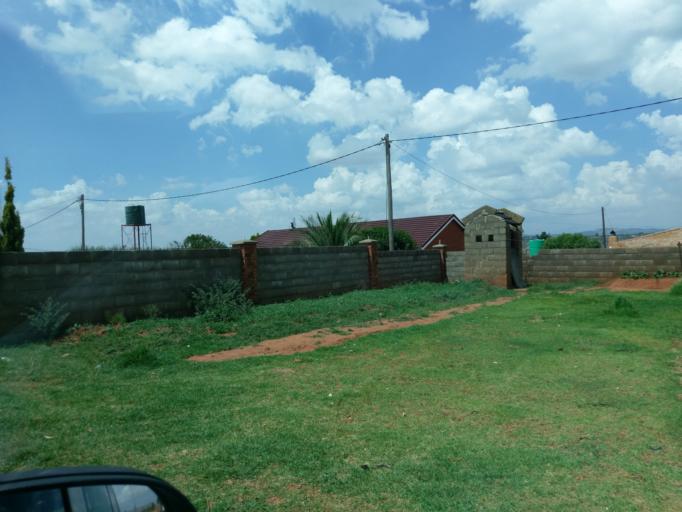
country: LS
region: Maseru
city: Maseru
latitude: -29.4208
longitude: 27.5672
